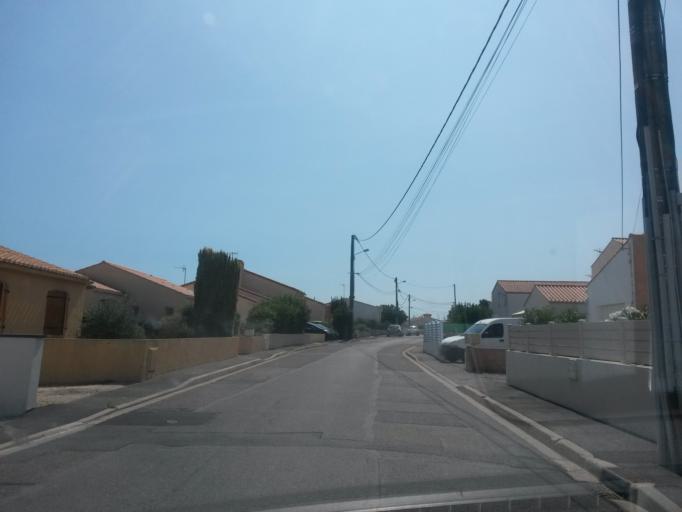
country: FR
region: Pays de la Loire
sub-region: Departement de la Vendee
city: Les Sables-d'Olonne
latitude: 46.5110
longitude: -1.8077
